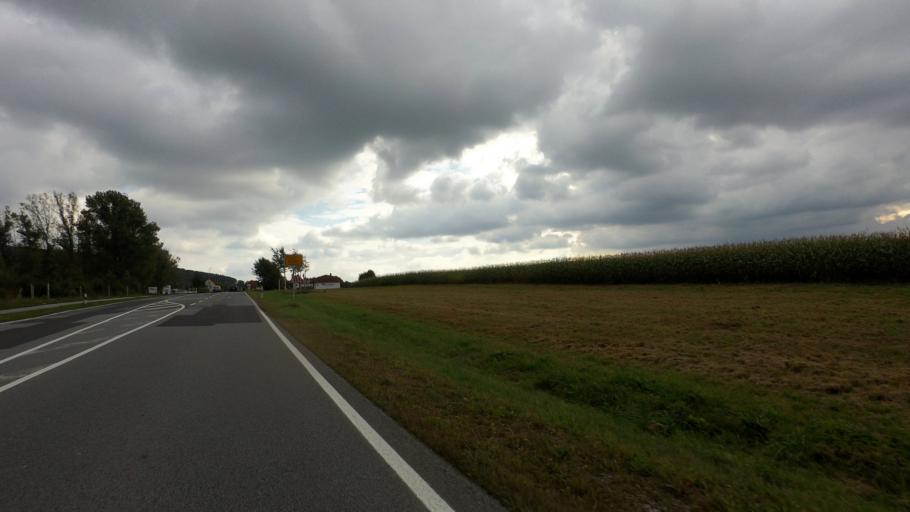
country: DE
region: Saxony
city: Grosspostwitz
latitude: 51.1454
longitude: 14.4398
